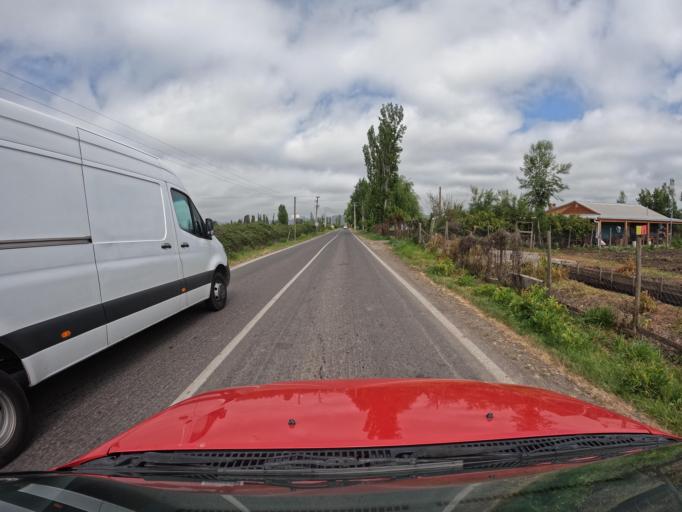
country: CL
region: O'Higgins
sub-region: Provincia de Colchagua
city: Santa Cruz
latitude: -34.6771
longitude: -71.3569
